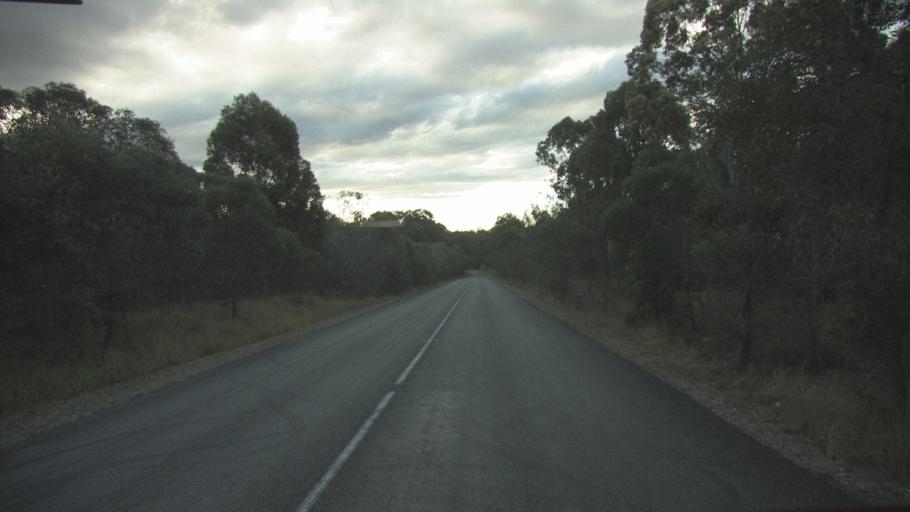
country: AU
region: Queensland
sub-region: Logan
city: Chambers Flat
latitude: -27.7969
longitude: 153.1415
